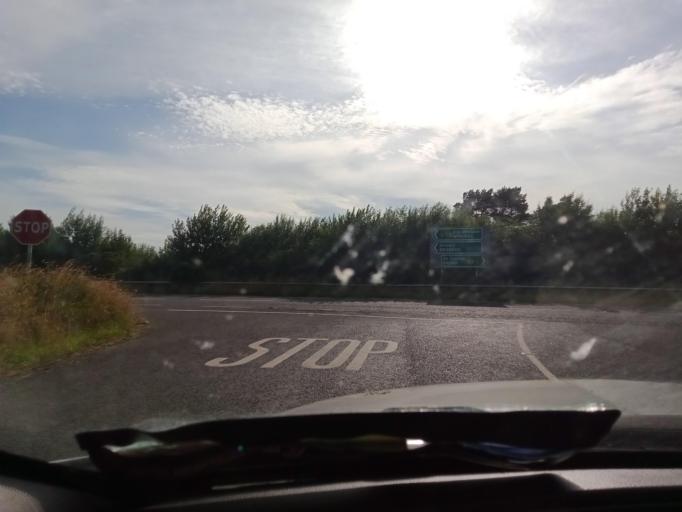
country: IE
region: Leinster
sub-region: An Longfort
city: Granard
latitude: 53.8460
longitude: -7.4490
